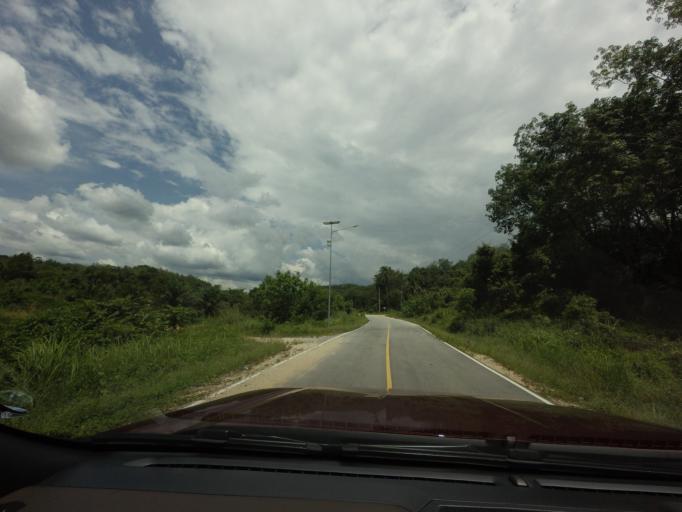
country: TH
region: Narathiwat
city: Chanae
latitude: 6.0557
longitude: 101.6876
